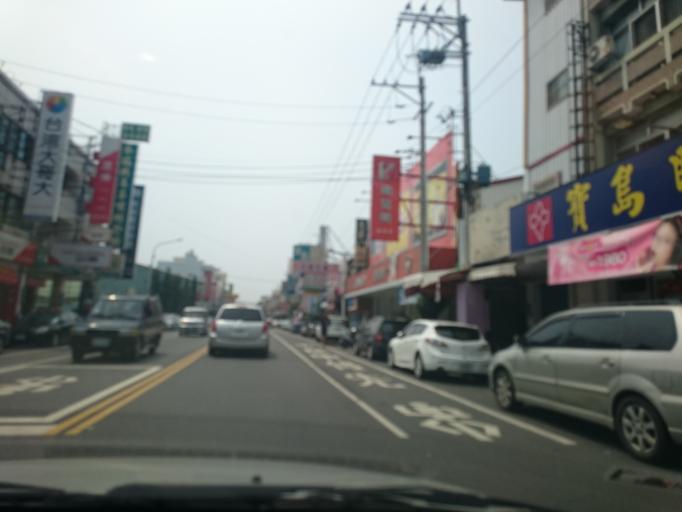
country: TW
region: Taiwan
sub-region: Nantou
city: Nantou
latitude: 23.8730
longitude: 120.5218
